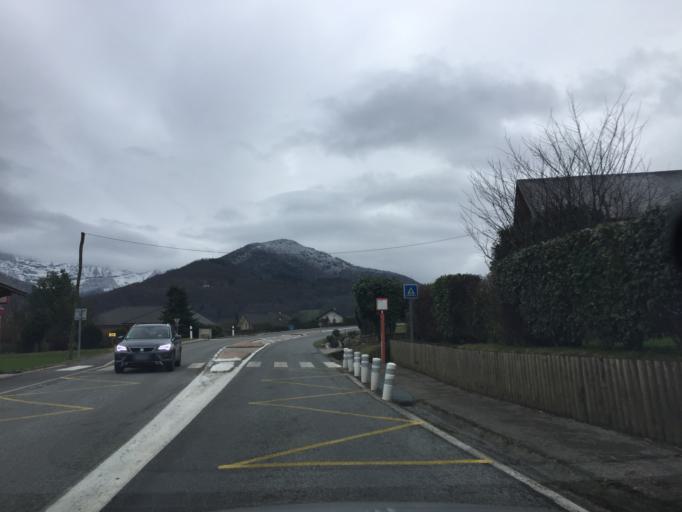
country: FR
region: Rhone-Alpes
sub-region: Departement de la Savoie
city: Cognin
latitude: 45.5501
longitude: 5.8844
